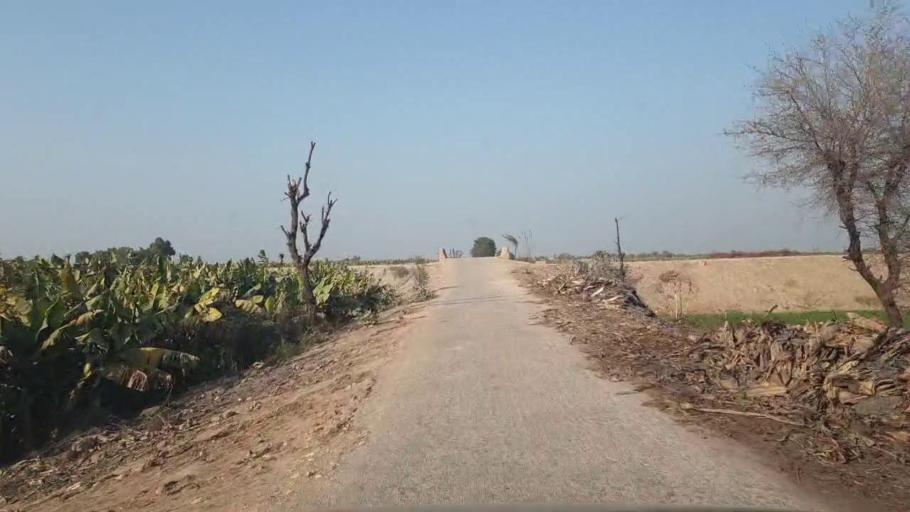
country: PK
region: Sindh
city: Bhit Shah
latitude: 25.8157
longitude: 68.5139
